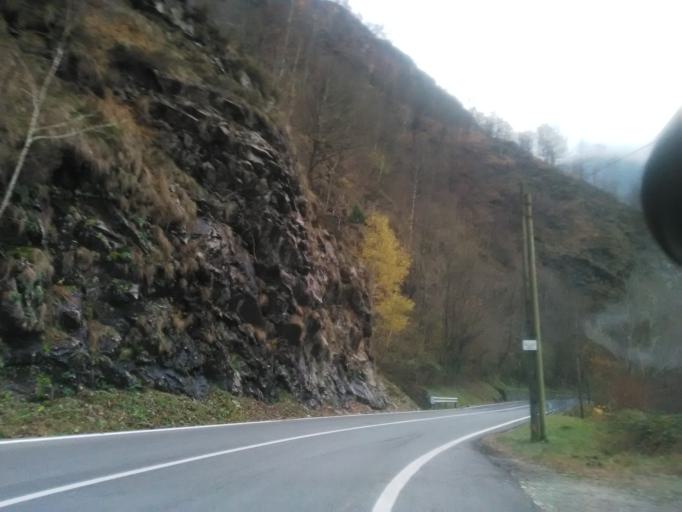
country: IT
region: Piedmont
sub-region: Provincia di Vercelli
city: Sabbia
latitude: 45.8518
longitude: 8.2431
